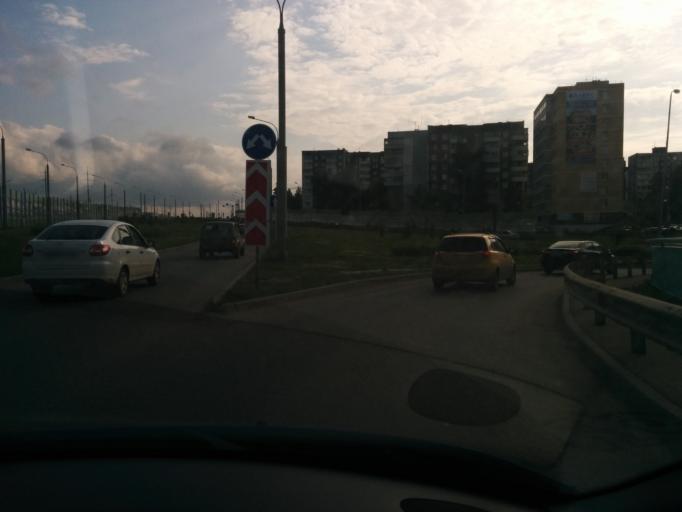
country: RU
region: Perm
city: Perm
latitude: 58.0011
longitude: 56.3148
